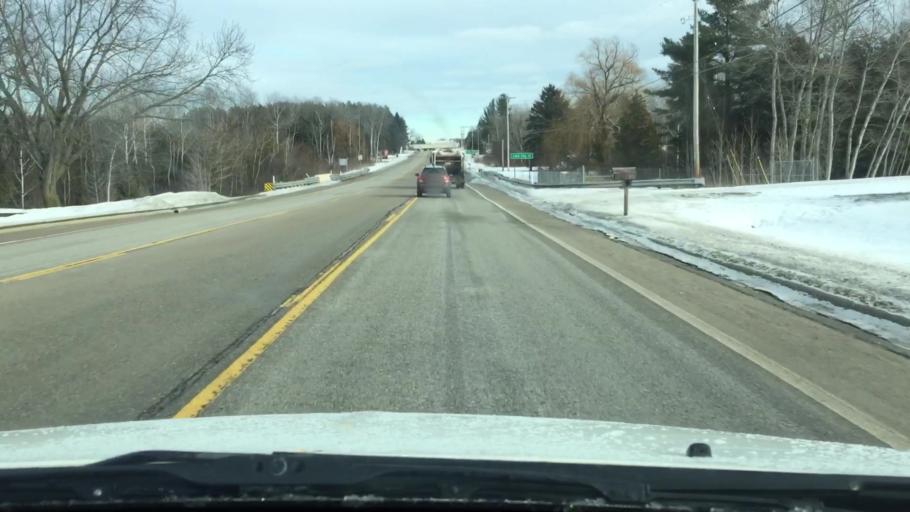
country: US
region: Michigan
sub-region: Wexford County
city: Manton
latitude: 44.4037
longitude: -85.3941
